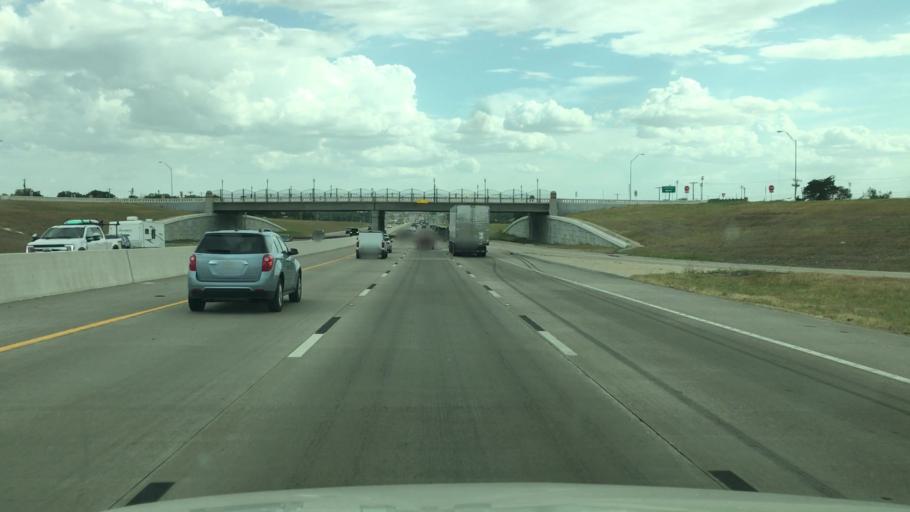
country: US
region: Texas
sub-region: McLennan County
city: Lorena
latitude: 31.3820
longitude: -97.2136
